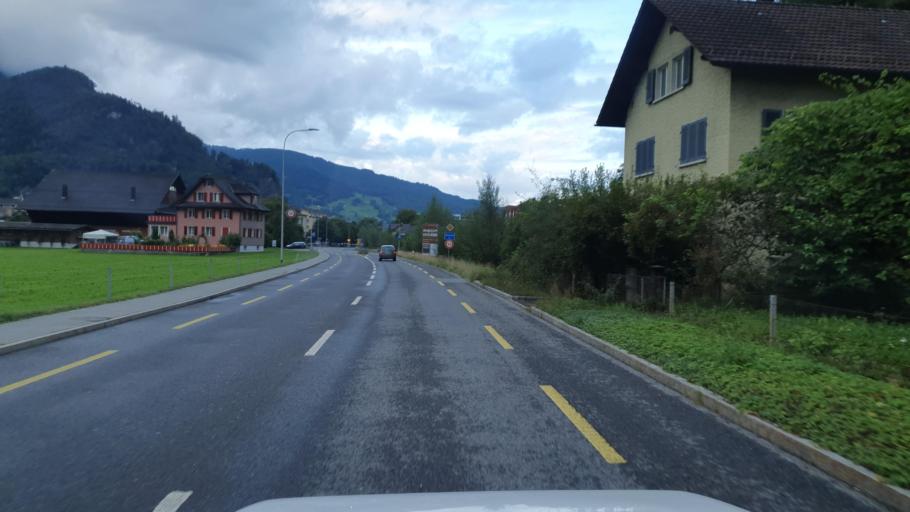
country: CH
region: Nidwalden
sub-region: Nidwalden
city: Stansstad
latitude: 46.9732
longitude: 8.3470
